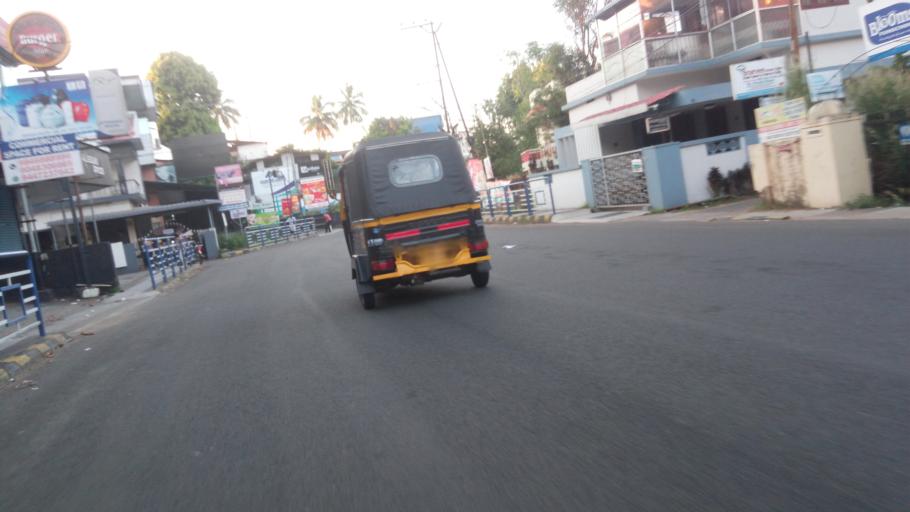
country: IN
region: Kerala
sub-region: Thrissur District
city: Trichur
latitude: 10.5369
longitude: 76.2122
